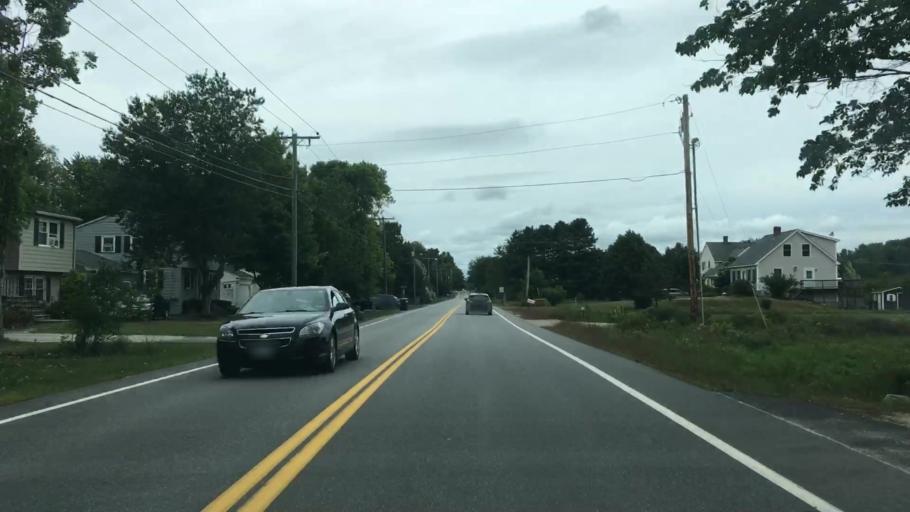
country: US
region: Maine
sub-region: Cumberland County
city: Yarmouth
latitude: 43.8191
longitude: -70.1862
